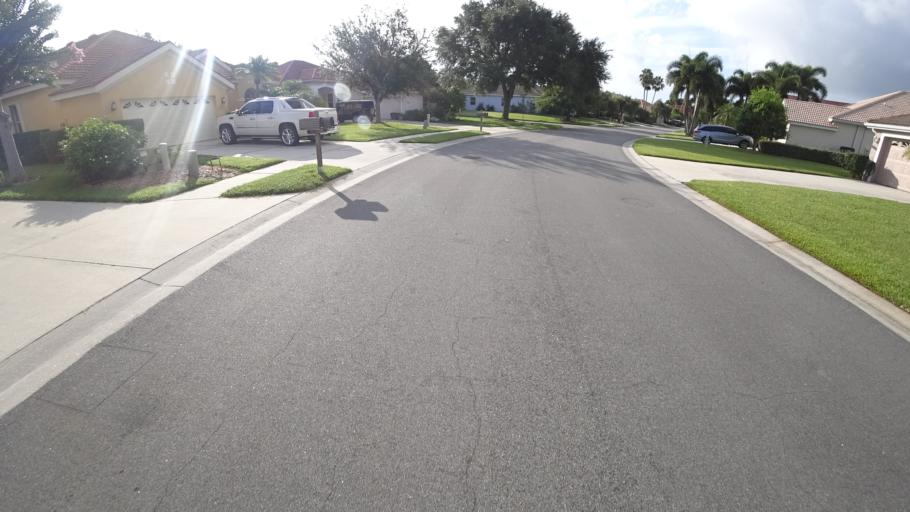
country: US
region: Florida
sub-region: Sarasota County
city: Desoto Lakes
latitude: 27.4212
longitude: -82.4878
